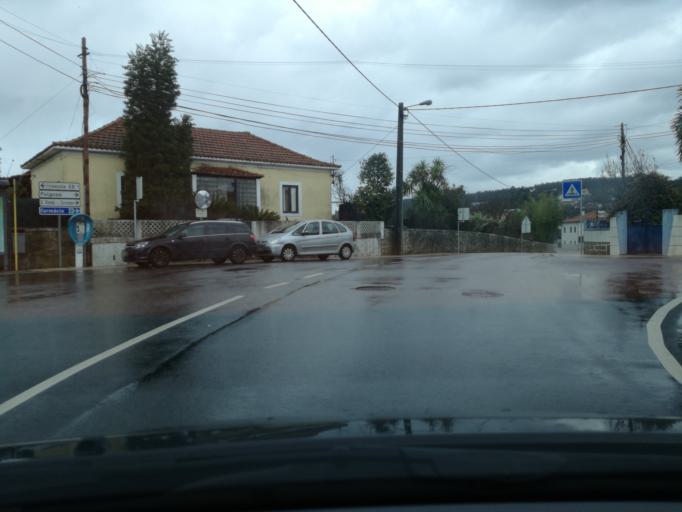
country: PT
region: Porto
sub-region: Valongo
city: Alfena
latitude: 41.2507
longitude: -8.5482
